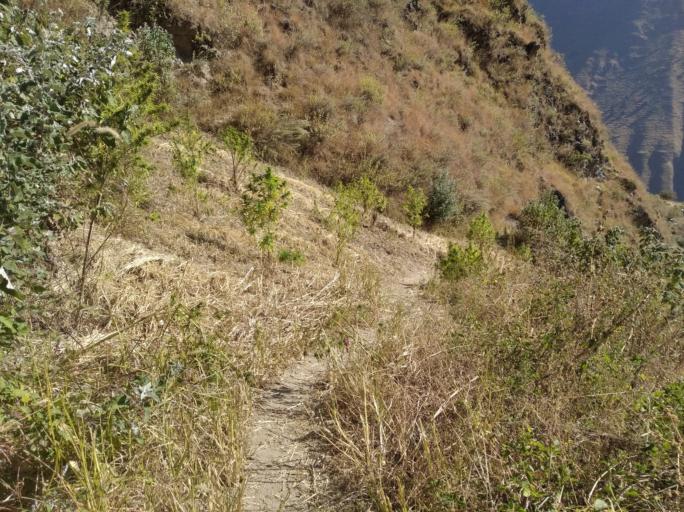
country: NP
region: Western Region
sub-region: Dhawalagiri Zone
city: Jomsom
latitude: 28.8884
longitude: 82.9726
